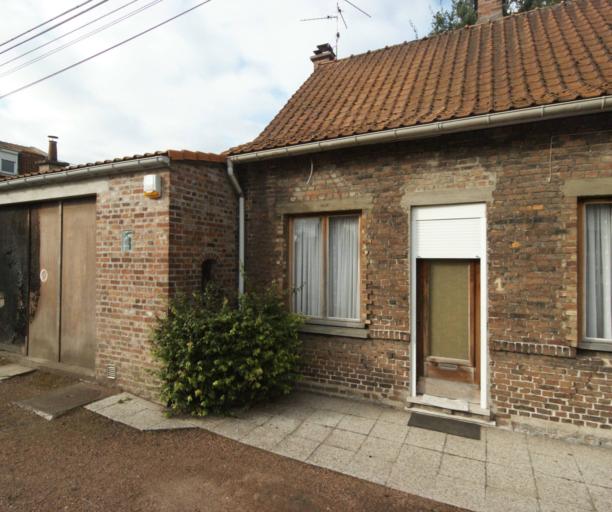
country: FR
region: Nord-Pas-de-Calais
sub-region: Departement du Nord
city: Hem
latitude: 50.6672
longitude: 3.1873
